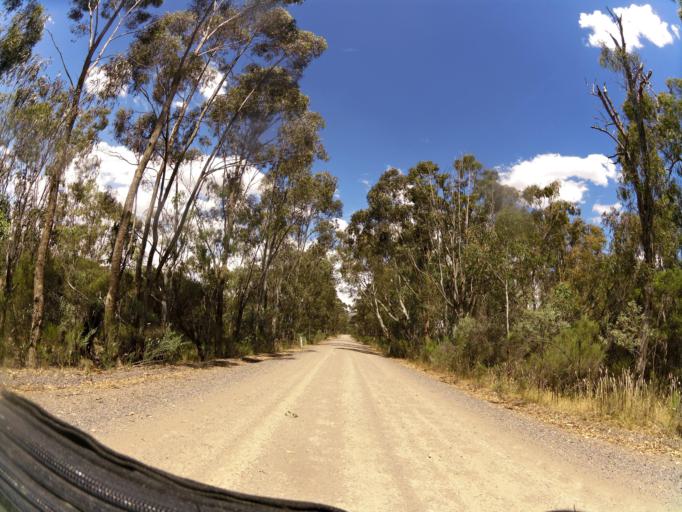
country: AU
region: Victoria
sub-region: Campaspe
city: Kyabram
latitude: -36.8108
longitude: 145.0744
